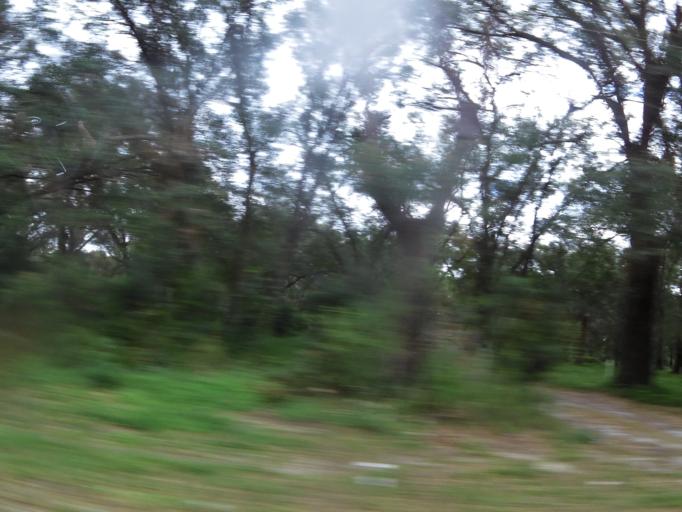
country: US
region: Florida
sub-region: Volusia County
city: Pierson
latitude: 29.3302
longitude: -81.4965
